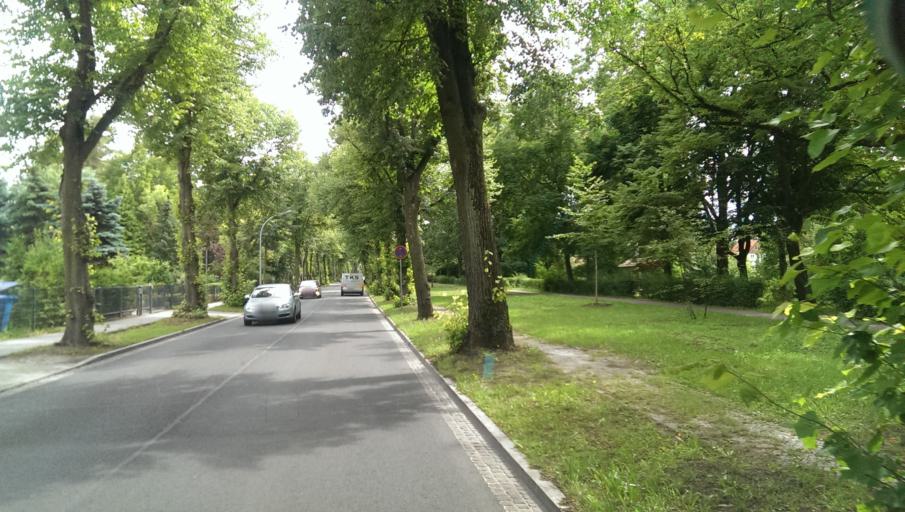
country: DE
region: Brandenburg
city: Kleinmachnow
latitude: 52.4197
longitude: 13.2255
